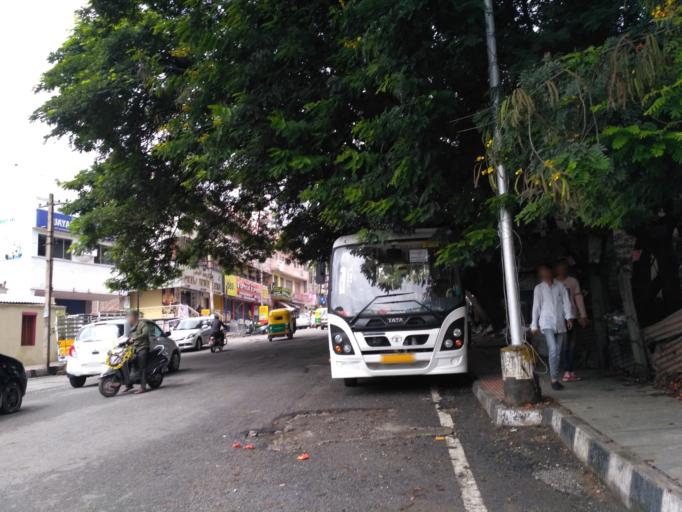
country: IN
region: Karnataka
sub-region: Bangalore Urban
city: Bangalore
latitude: 12.9600
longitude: 77.5326
